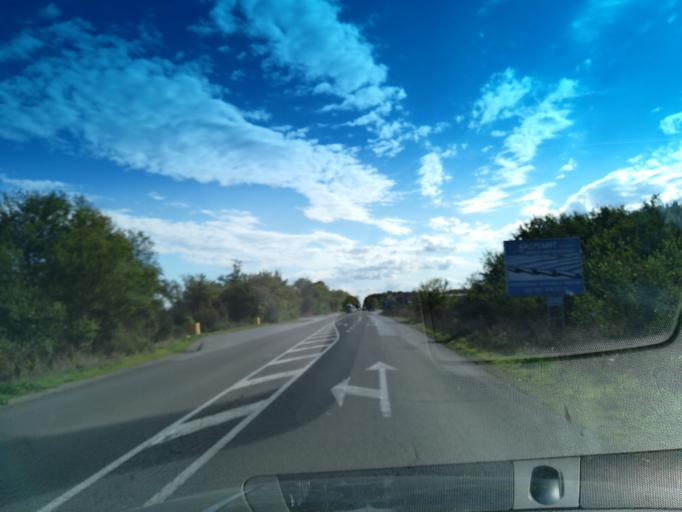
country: BG
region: Stara Zagora
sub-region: Obshtina Stara Zagora
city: Stara Zagora
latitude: 42.3584
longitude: 25.6566
